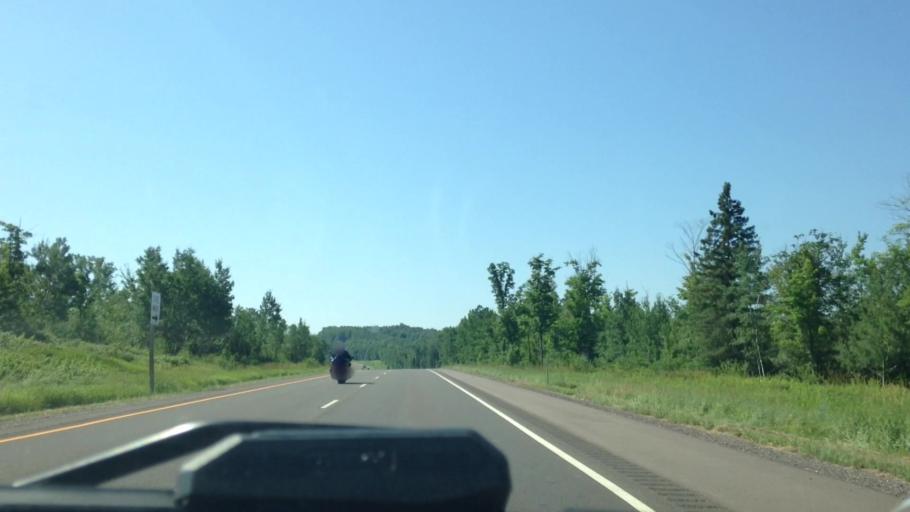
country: US
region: Wisconsin
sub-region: Washburn County
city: Spooner
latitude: 46.0183
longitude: -91.8383
